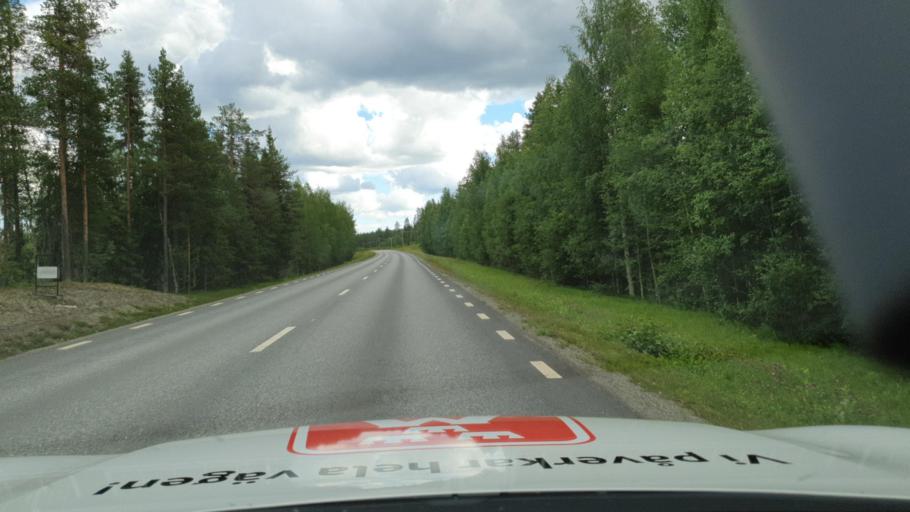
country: SE
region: Vaesterbotten
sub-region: Lycksele Kommun
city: Soderfors
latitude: 64.8993
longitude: 17.8753
